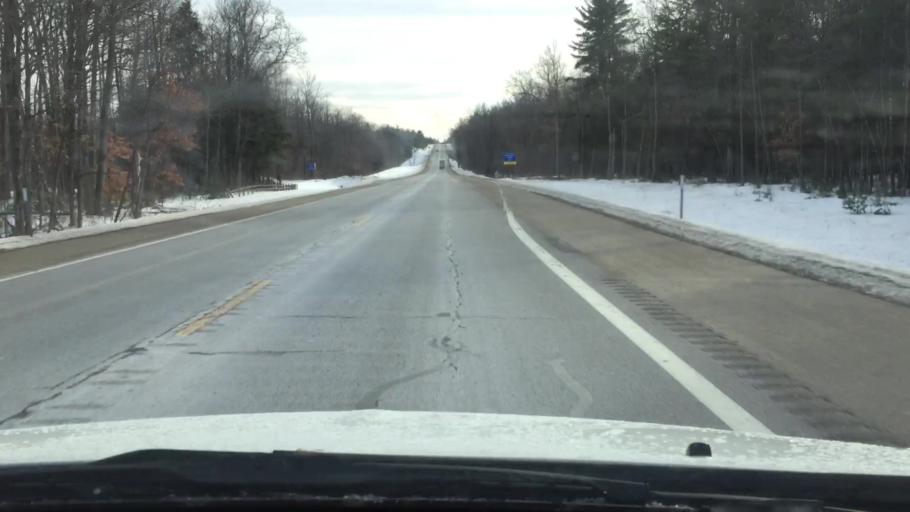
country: US
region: Michigan
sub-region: Wexford County
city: Manton
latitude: 44.4905
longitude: -85.4062
